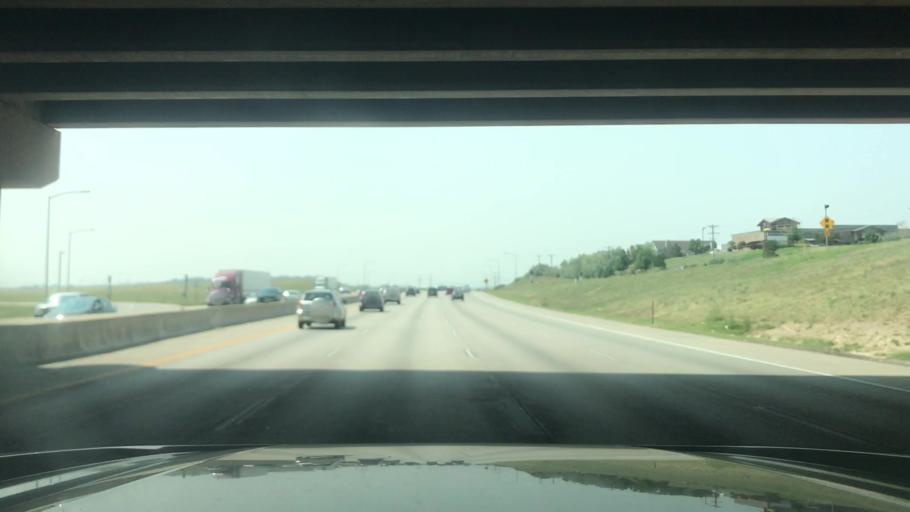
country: US
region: Colorado
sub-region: Park County
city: Castle Pines North
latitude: 39.4721
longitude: -104.8728
